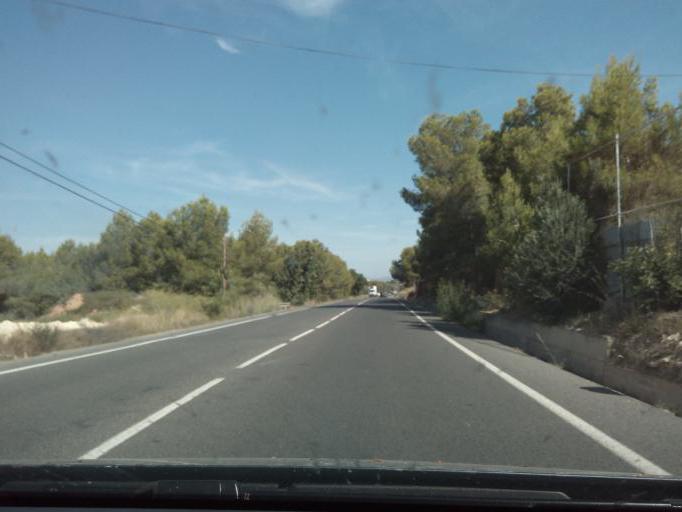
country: ES
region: Valencia
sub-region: Provincia de Valencia
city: Manises
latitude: 39.5356
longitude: -0.4751
